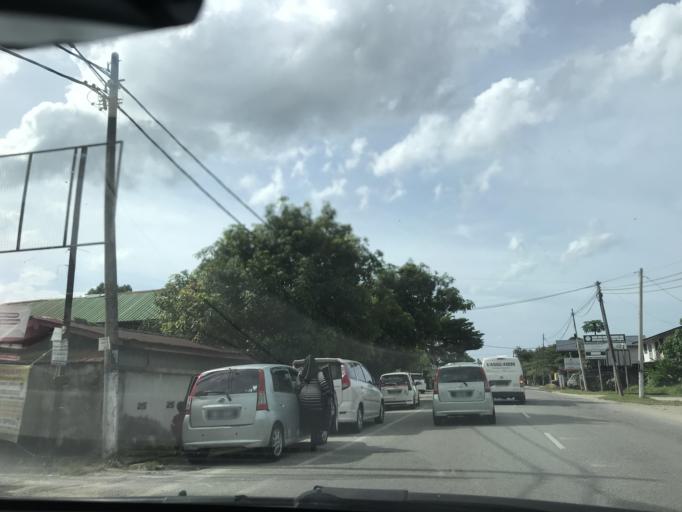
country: MY
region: Kelantan
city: Kota Bharu
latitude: 6.0853
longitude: 102.2274
